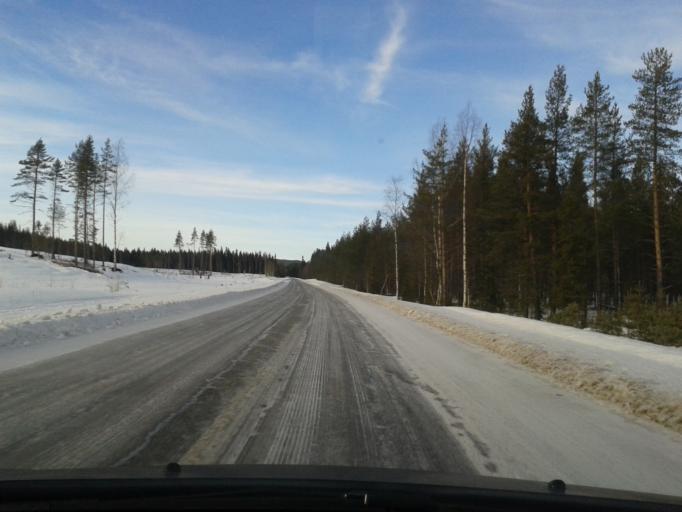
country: SE
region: Vaesternorrland
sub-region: OErnskoeldsviks Kommun
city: Bredbyn
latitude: 63.5953
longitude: 17.9174
